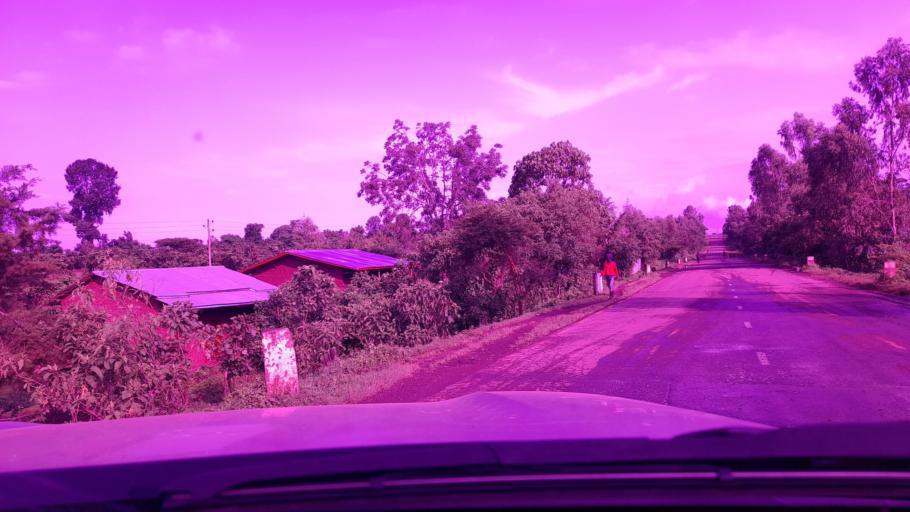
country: ET
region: Oromiya
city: Bedele
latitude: 8.1849
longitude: 36.4510
